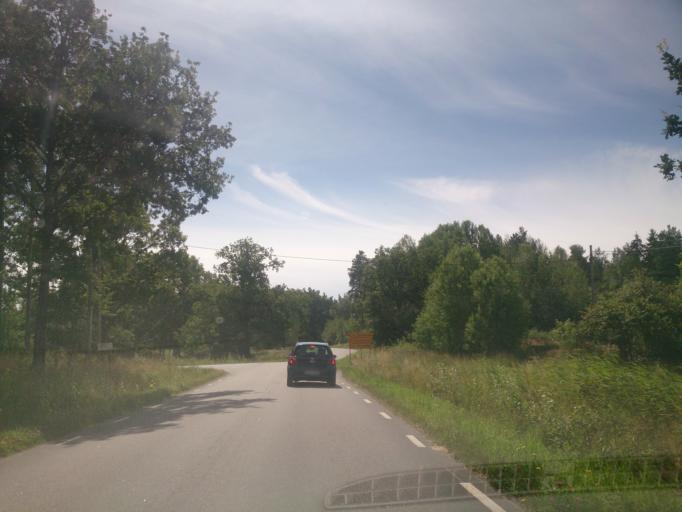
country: SE
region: OEstergoetland
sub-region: Valdemarsviks Kommun
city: Valdemarsvik
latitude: 58.3202
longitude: 16.6489
